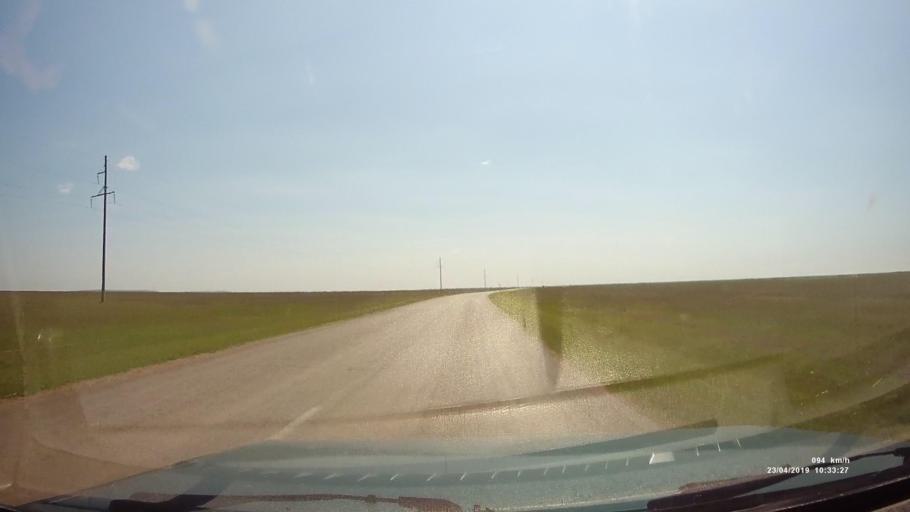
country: RU
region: Kalmykiya
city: Yashalta
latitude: 46.5734
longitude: 42.5968
